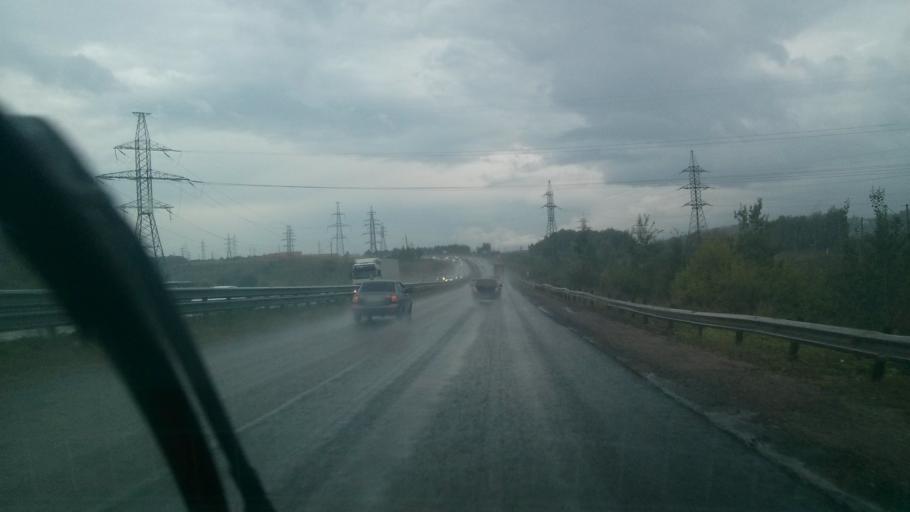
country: RU
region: Nizjnij Novgorod
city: Afonino
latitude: 56.2335
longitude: 44.0593
